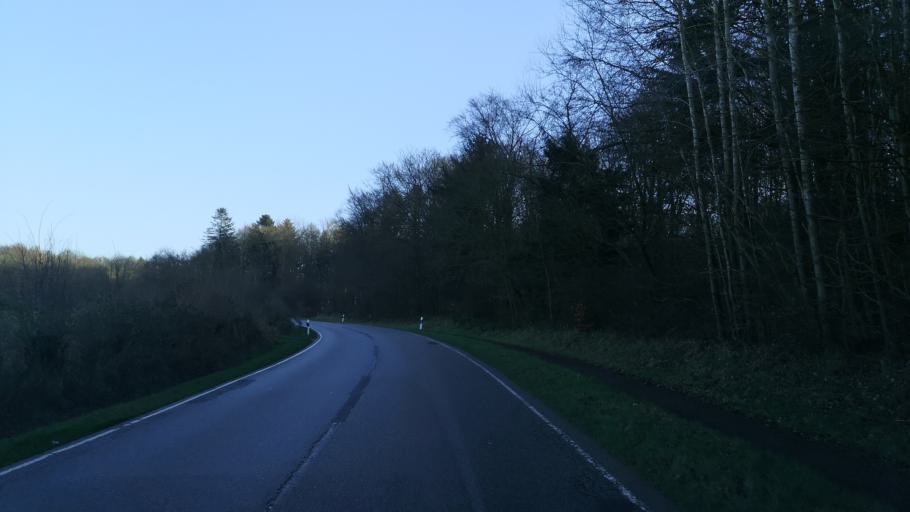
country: DE
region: Schleswig-Holstein
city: Grosssolt
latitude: 54.6974
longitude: 9.5502
